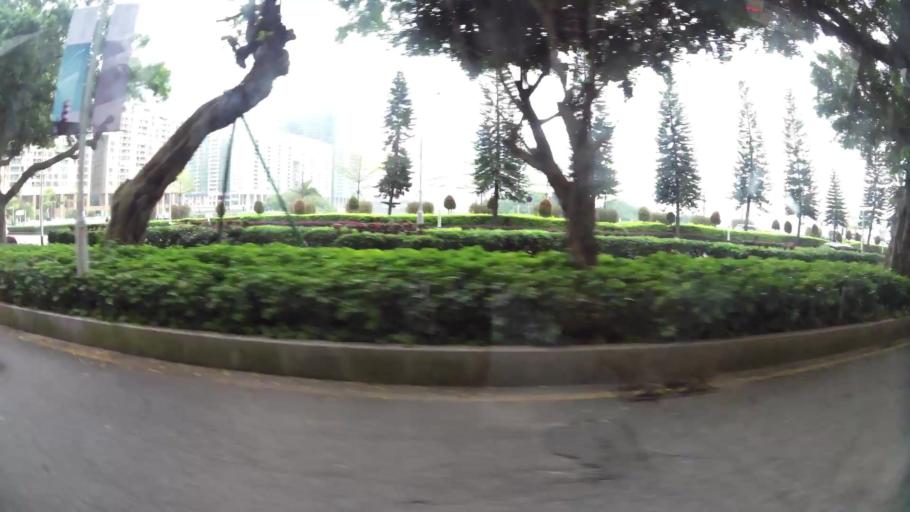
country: MO
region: Macau
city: Macau
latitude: 22.1890
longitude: 113.5379
